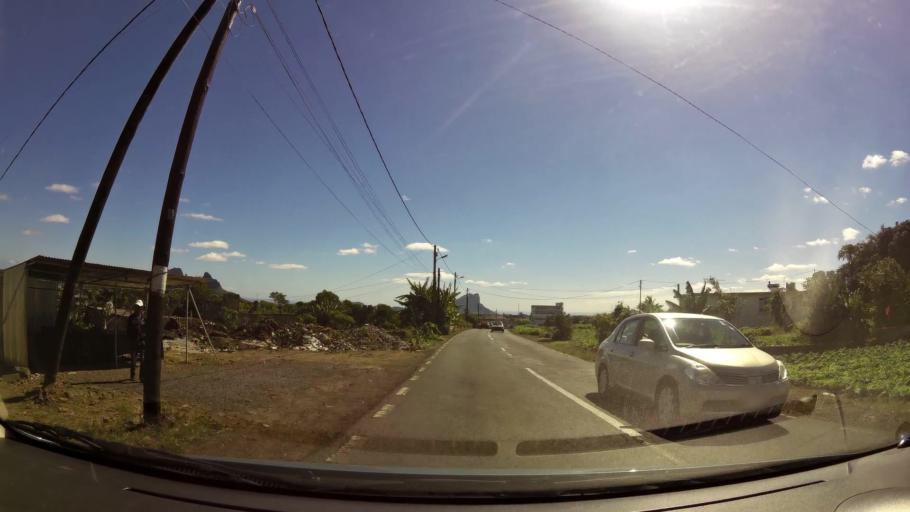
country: MU
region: Plaines Wilhems
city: Vacoas
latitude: -20.3327
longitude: 57.4874
